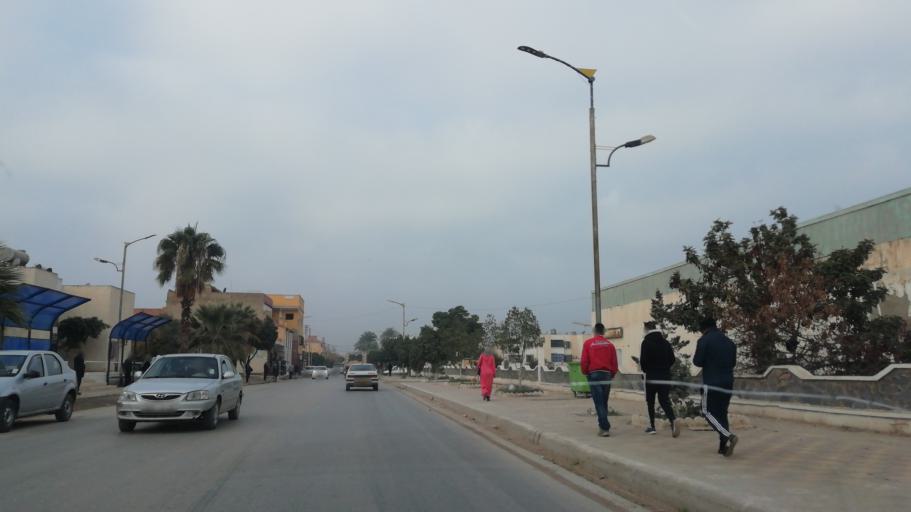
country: DZ
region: Relizane
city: Djidiouia
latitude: 35.9296
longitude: 0.8354
